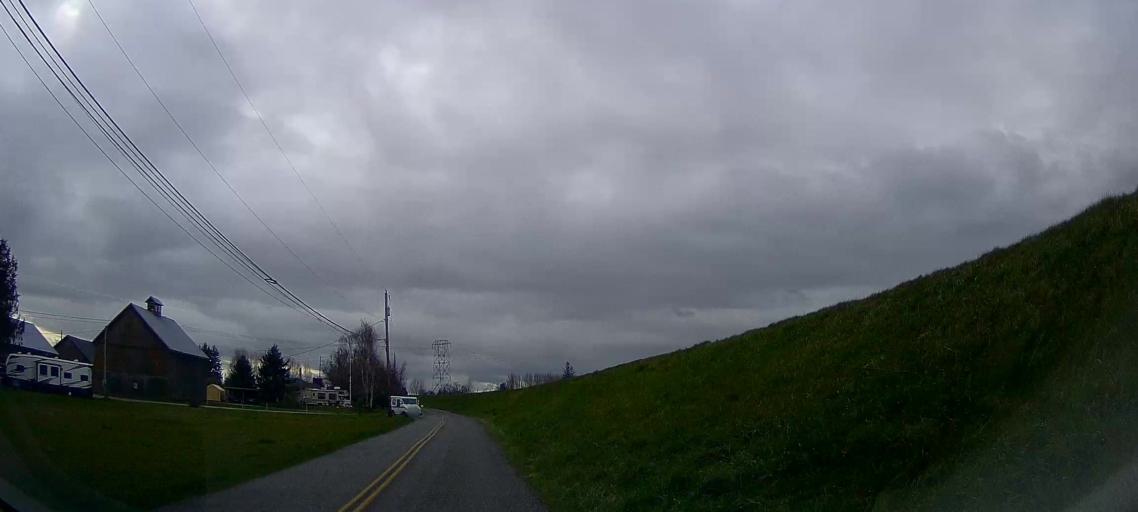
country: US
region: Washington
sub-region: Skagit County
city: Mount Vernon
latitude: 48.4438
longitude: -122.3700
